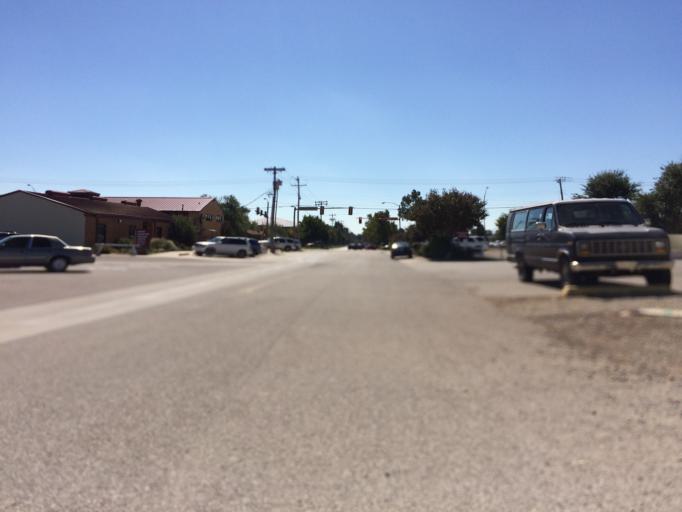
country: US
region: Oklahoma
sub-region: Cleveland County
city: Norman
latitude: 35.2339
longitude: -97.4375
